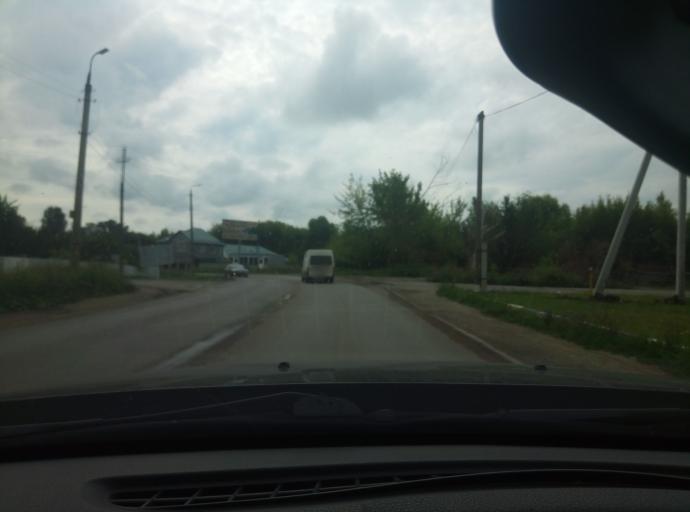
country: RU
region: Tula
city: Donskoy
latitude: 53.9686
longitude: 38.3580
